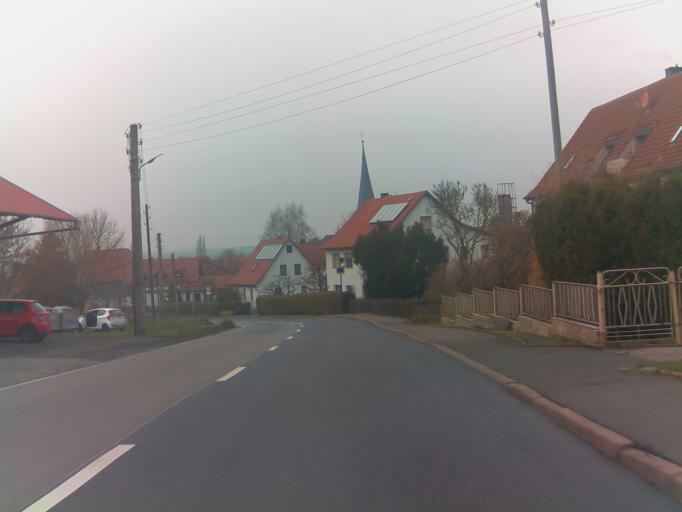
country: DE
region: Thuringia
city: Wolfershausen
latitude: 50.4289
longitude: 10.4627
